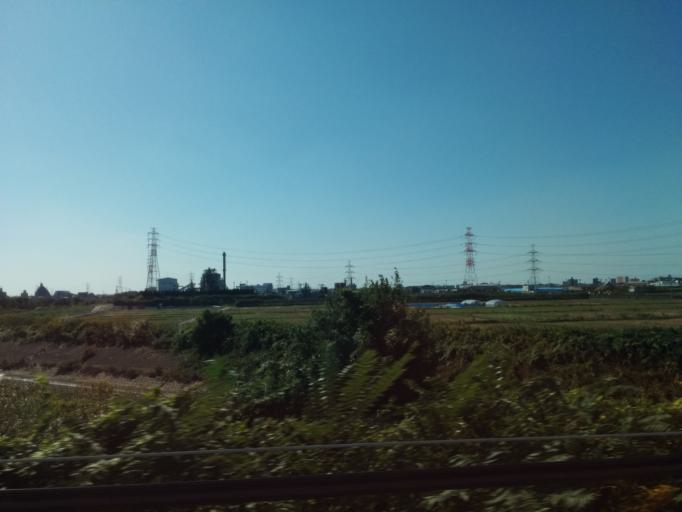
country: JP
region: Aichi
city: Obu
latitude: 35.0181
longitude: 136.9952
